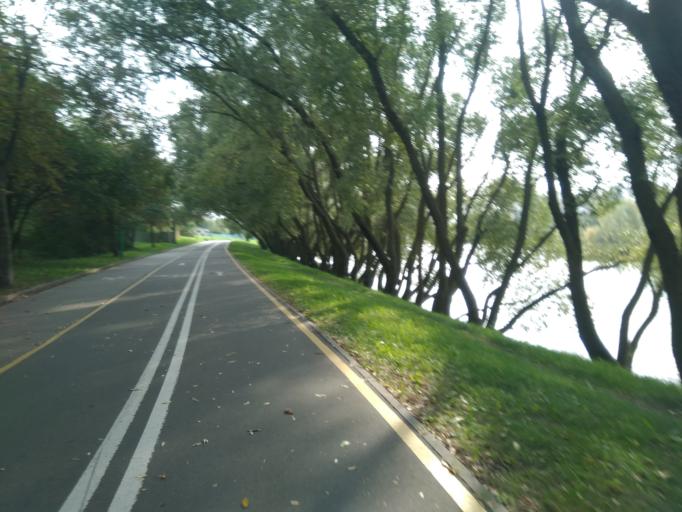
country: BY
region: Minsk
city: Minsk
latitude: 53.8802
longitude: 27.5753
